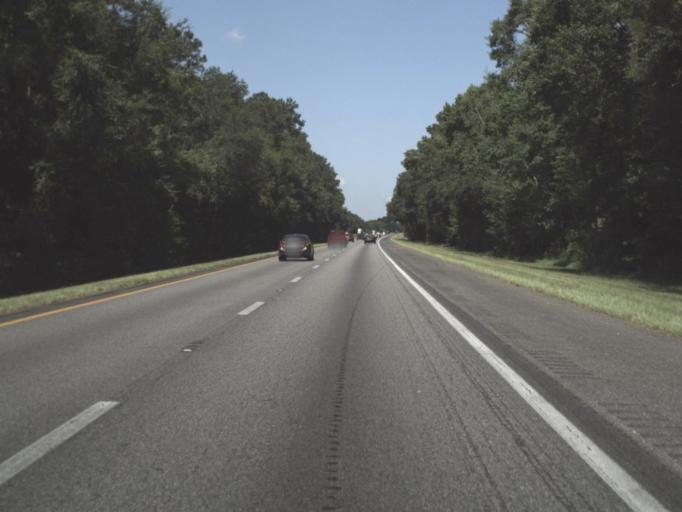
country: US
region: Florida
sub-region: Madison County
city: Madison
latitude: 30.4307
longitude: -83.5612
